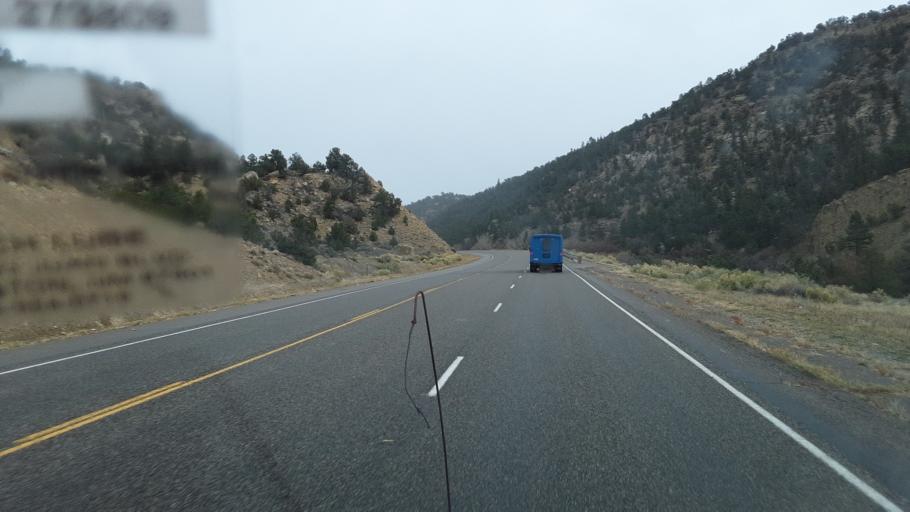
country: US
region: New Mexico
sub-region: Rio Arriba County
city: Tierra Amarilla
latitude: 36.4131
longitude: -106.4834
